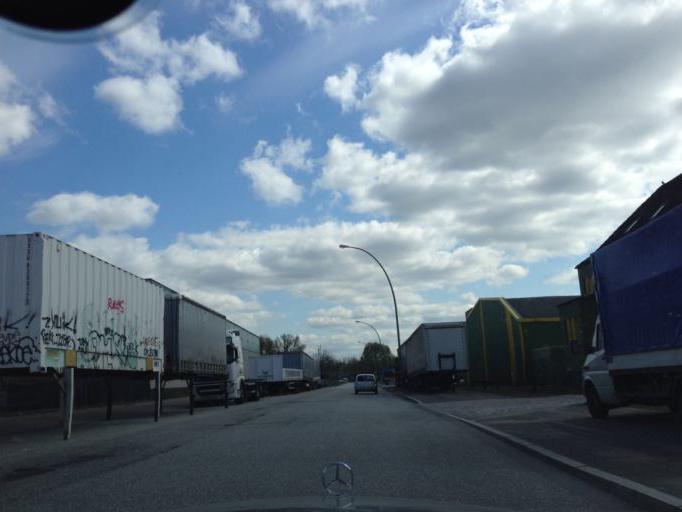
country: DE
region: Hamburg
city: Wandsbek
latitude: 53.5312
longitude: 10.1031
